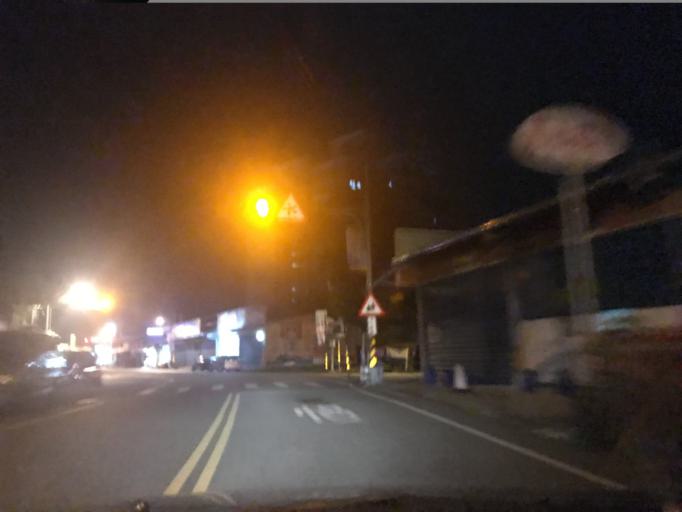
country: TW
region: Taiwan
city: Daxi
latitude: 24.8588
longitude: 121.2176
